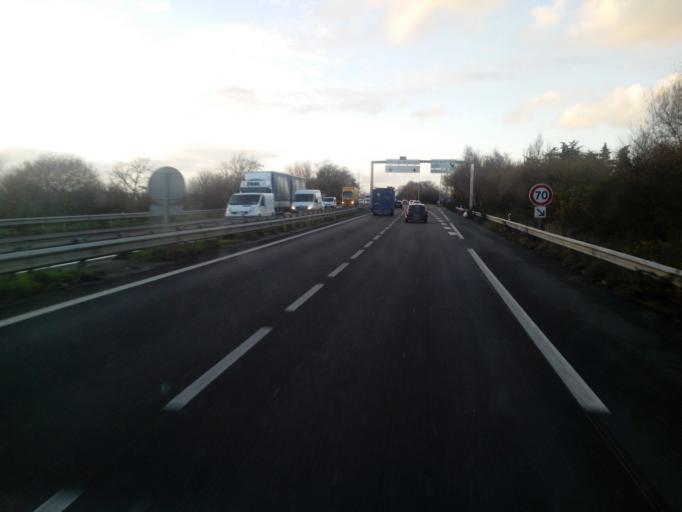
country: FR
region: Pays de la Loire
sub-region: Departement de la Loire-Atlantique
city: Sainte-Luce-sur-Loire
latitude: 47.2445
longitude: -1.4957
